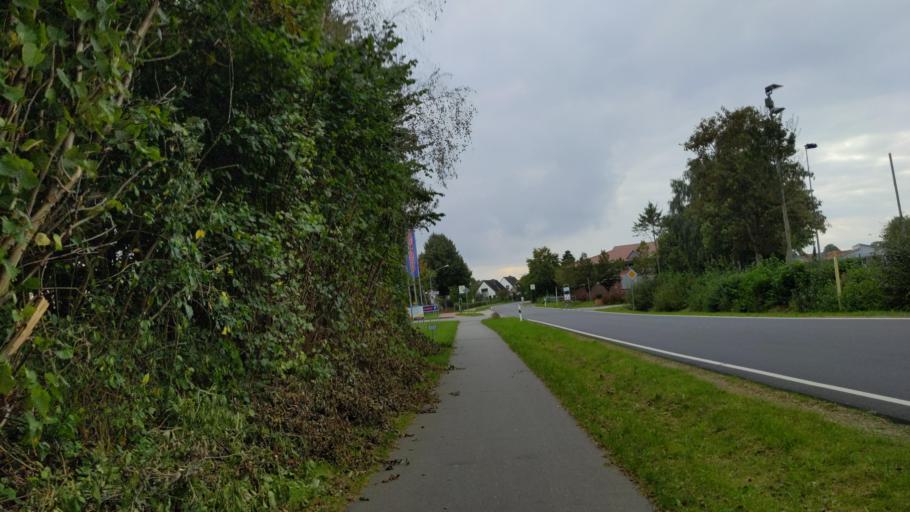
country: DE
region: Schleswig-Holstein
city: Krummesse
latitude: 53.7811
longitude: 10.6516
